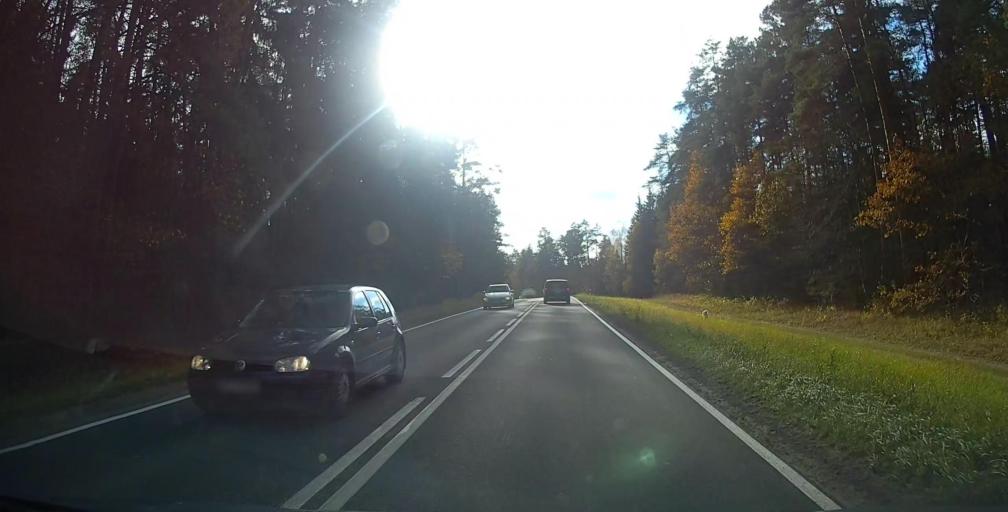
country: PL
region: Warmian-Masurian Voivodeship
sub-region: Powiat elcki
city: Elk
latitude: 53.7836
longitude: 22.3488
